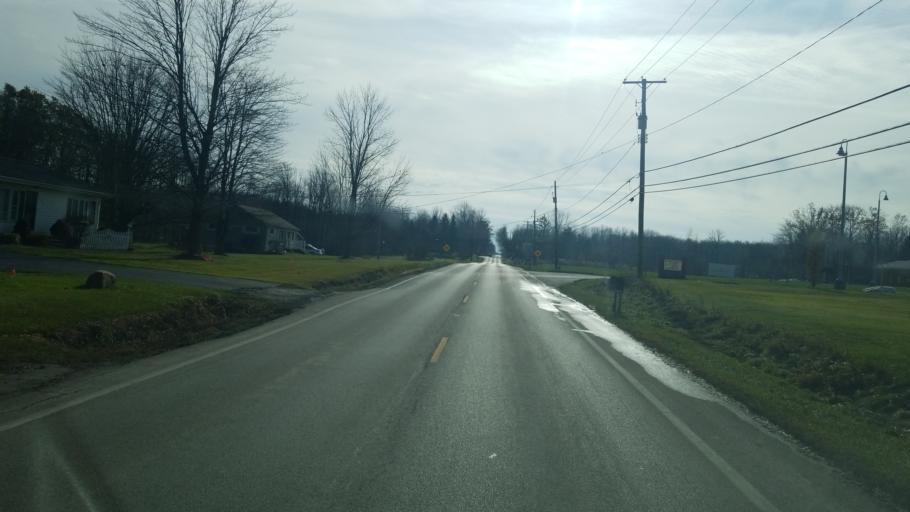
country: US
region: Ohio
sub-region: Ashtabula County
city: Geneva
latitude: 41.7342
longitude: -80.9524
